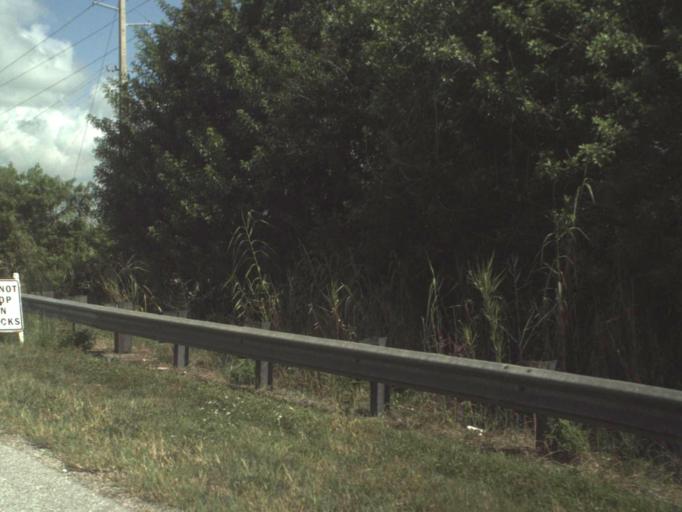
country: US
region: Florida
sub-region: Okeechobee County
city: Taylor Creek
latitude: 27.1420
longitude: -80.6515
